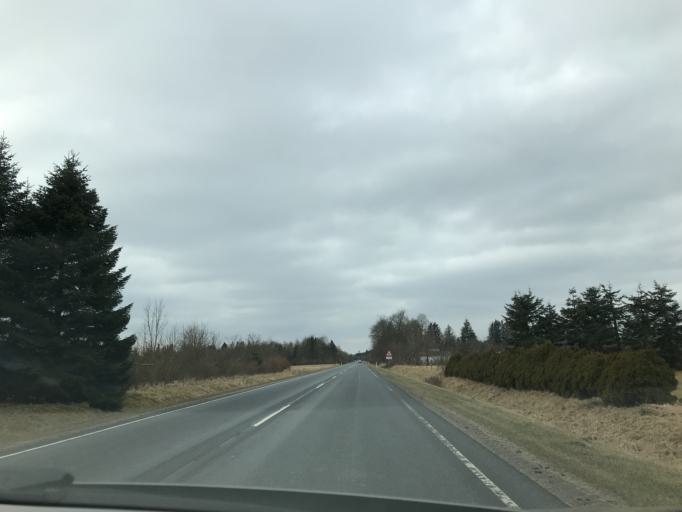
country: DK
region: South Denmark
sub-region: Billund Kommune
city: Grindsted
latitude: 55.8432
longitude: 8.8595
